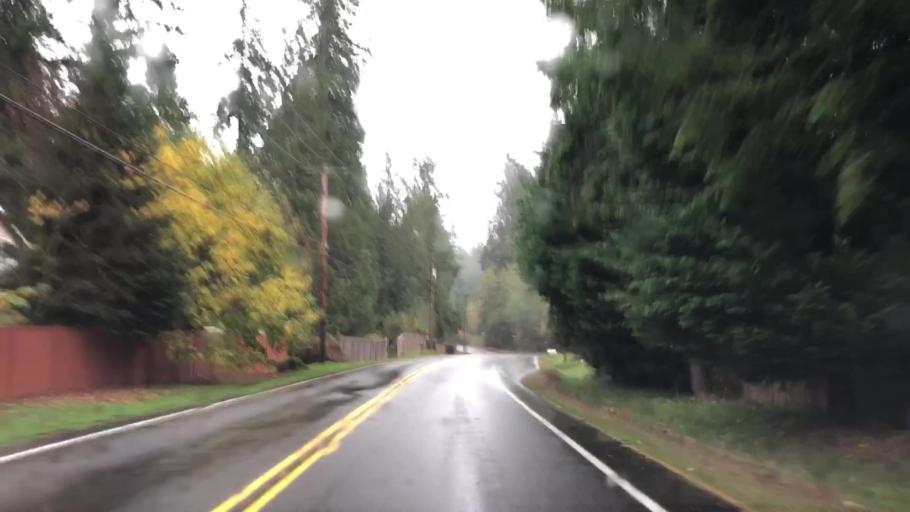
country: US
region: Washington
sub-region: King County
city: Cottage Lake
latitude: 47.7582
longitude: -122.1108
